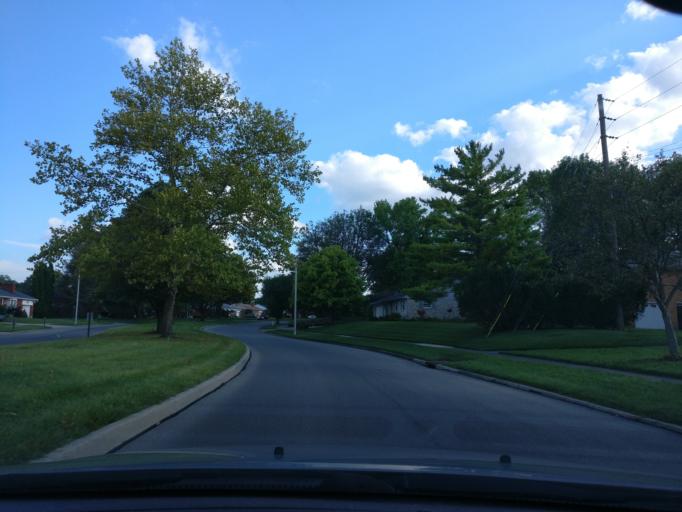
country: US
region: Ohio
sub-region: Montgomery County
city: Kettering
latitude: 39.6838
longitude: -84.1550
